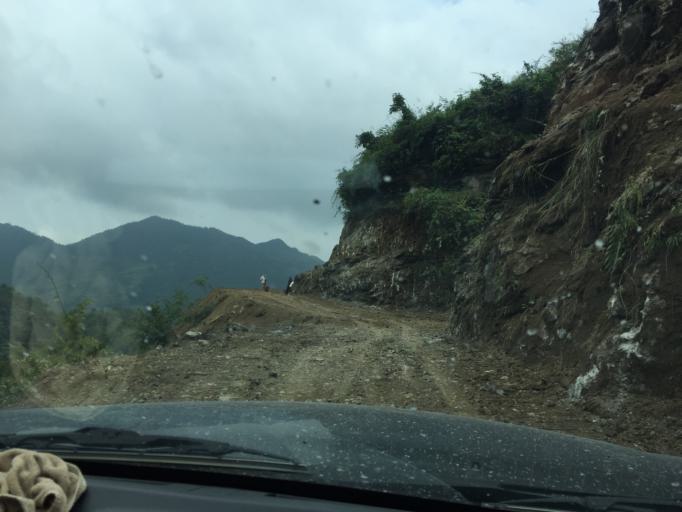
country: CN
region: Guizhou Sheng
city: Nangan
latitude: 28.2559
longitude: 107.9482
